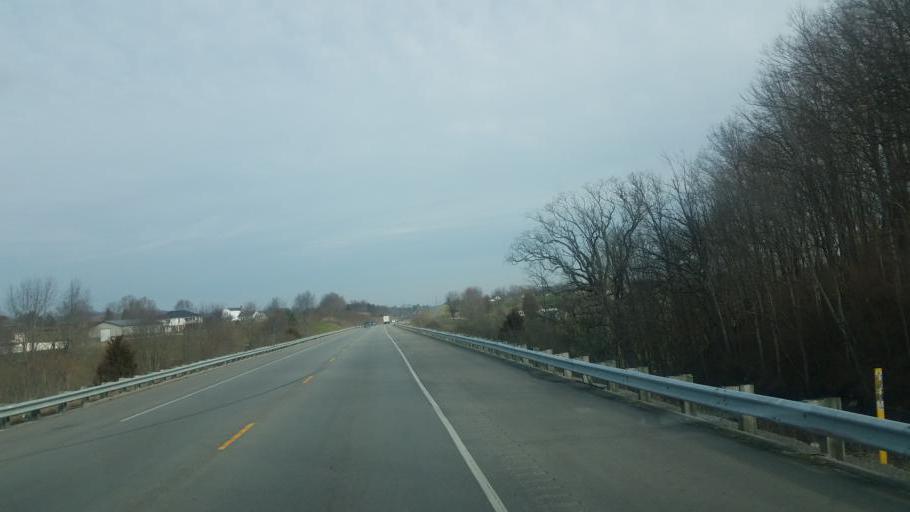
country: US
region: Kentucky
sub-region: Boyle County
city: Junction City
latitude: 37.5301
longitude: -84.8051
